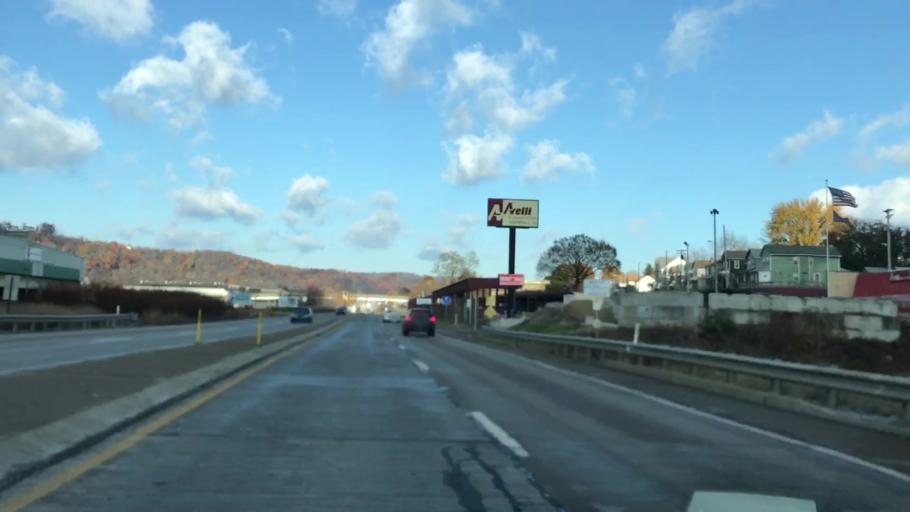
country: US
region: Pennsylvania
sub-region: Beaver County
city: Ambridge
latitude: 40.5776
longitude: -80.2234
